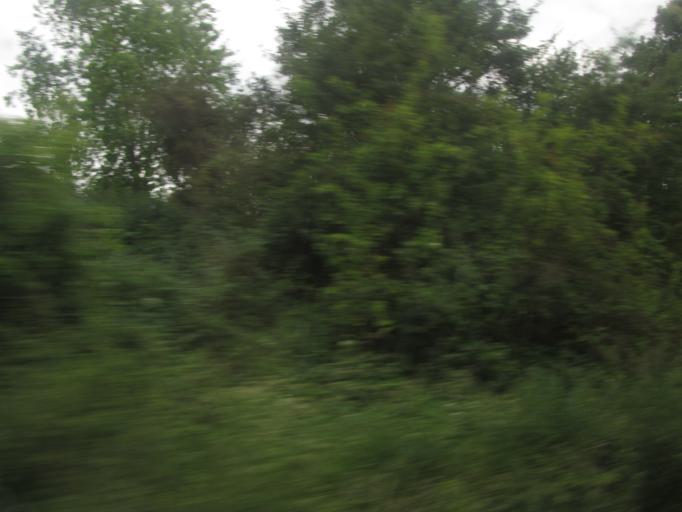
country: GB
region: England
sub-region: Northamptonshire
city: Desborough
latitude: 52.4447
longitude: -0.8068
